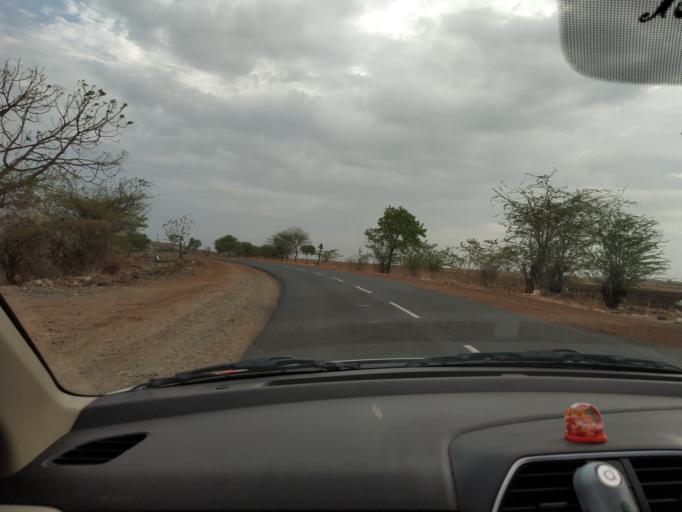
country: IN
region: Madhya Pradesh
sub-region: Shajapur
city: Agar
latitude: 23.6419
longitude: 75.9769
